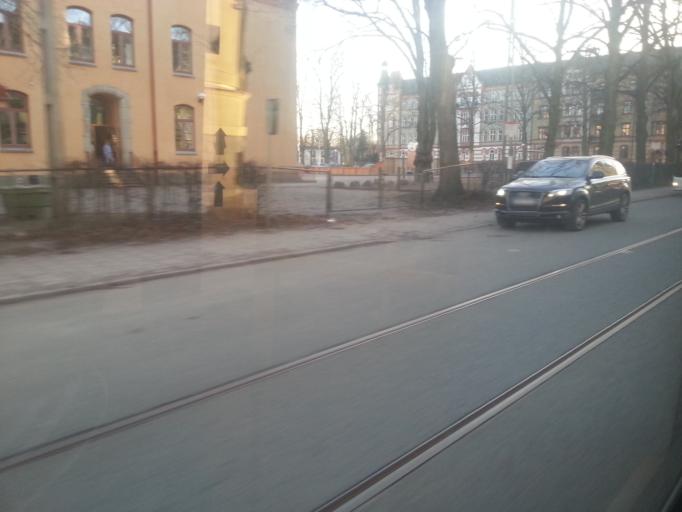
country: SE
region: OEstergoetland
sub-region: Norrkopings Kommun
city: Norrkoping
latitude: 58.5864
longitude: 16.1989
